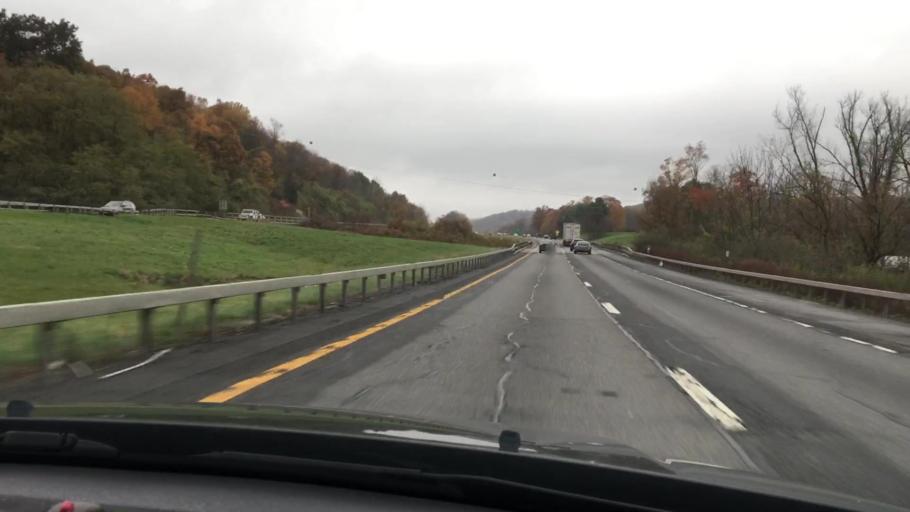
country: US
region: New York
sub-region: Putnam County
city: Lake Carmel
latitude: 41.4646
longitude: -73.6440
